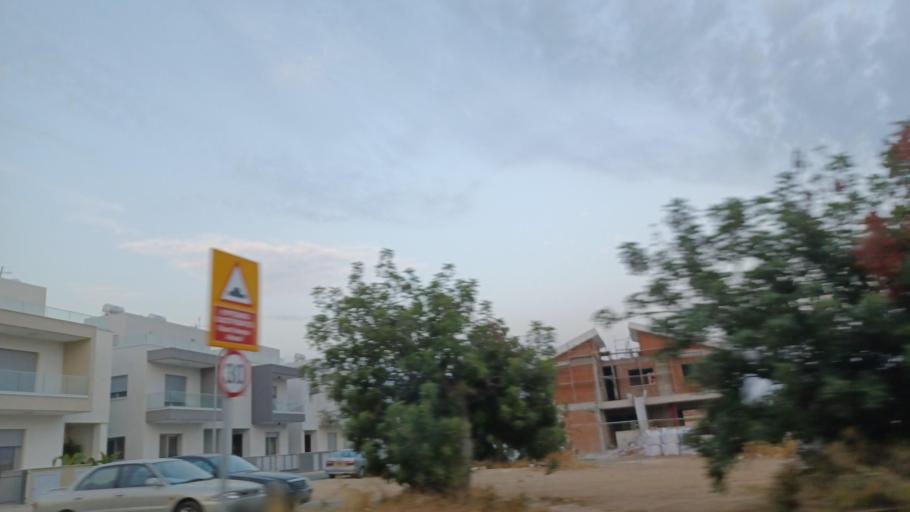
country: CY
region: Limassol
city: Ypsonas
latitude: 34.6912
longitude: 32.9667
